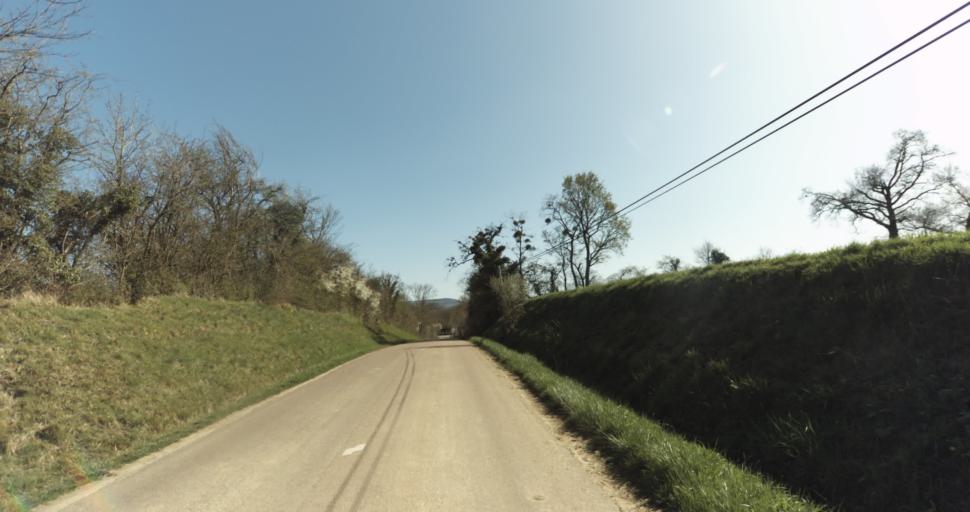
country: FR
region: Lower Normandy
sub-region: Departement du Calvados
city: Saint-Pierre-sur-Dives
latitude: 48.9429
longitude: 0.0178
